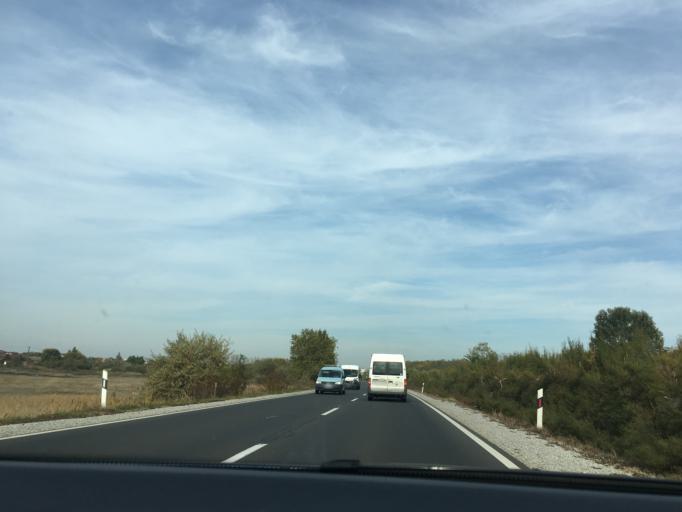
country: HU
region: Szabolcs-Szatmar-Bereg
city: Ujfeherto
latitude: 47.7993
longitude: 21.7029
